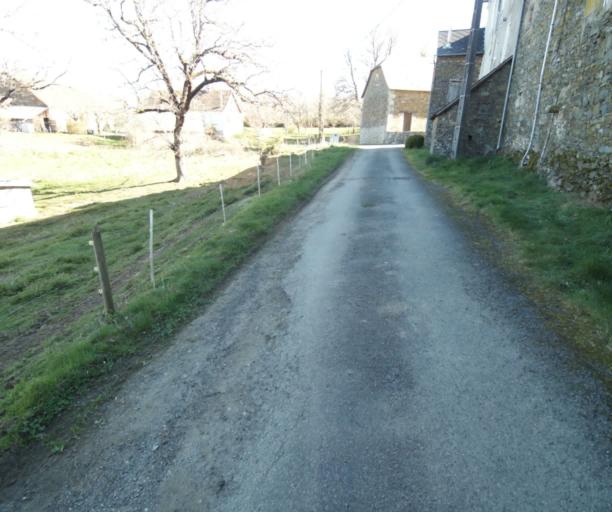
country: FR
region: Limousin
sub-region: Departement de la Correze
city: Seilhac
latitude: 45.3933
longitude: 1.7447
